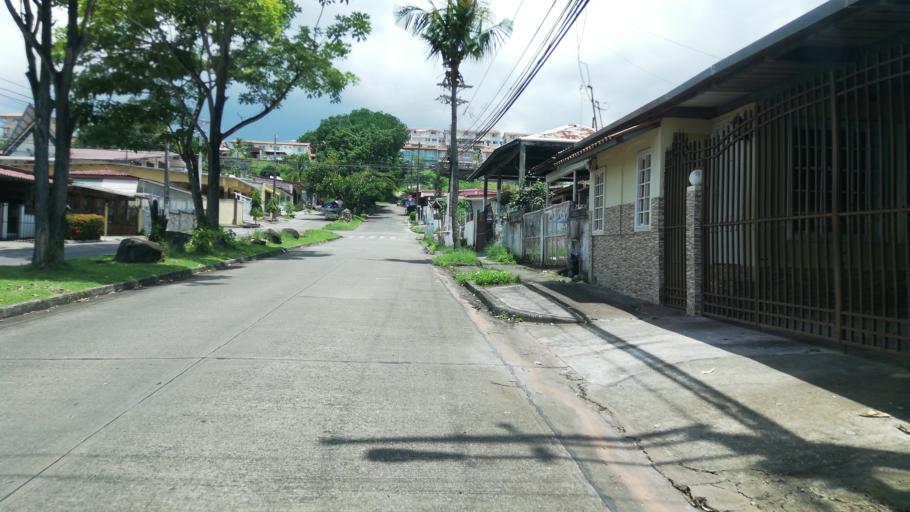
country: PA
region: Panama
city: San Miguelito
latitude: 9.0598
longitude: -79.4571
